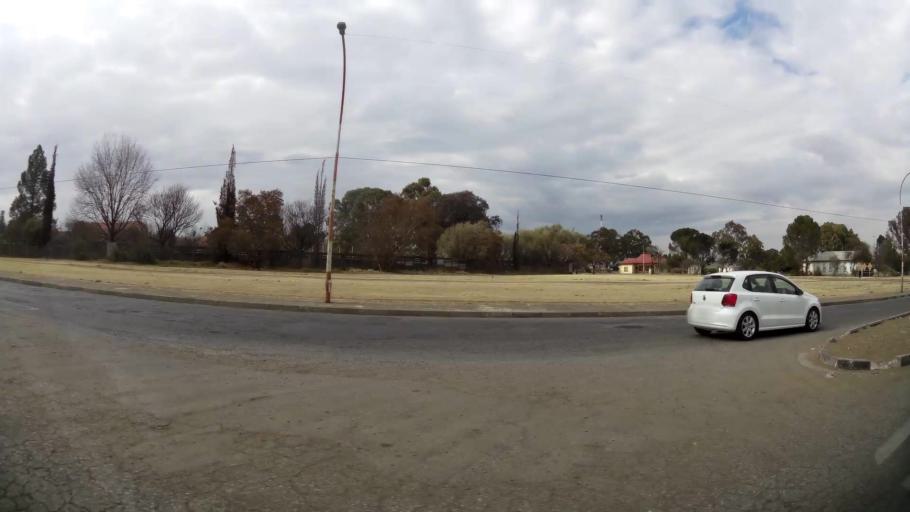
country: ZA
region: Orange Free State
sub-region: Fezile Dabi District Municipality
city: Kroonstad
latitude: -27.6571
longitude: 27.2302
